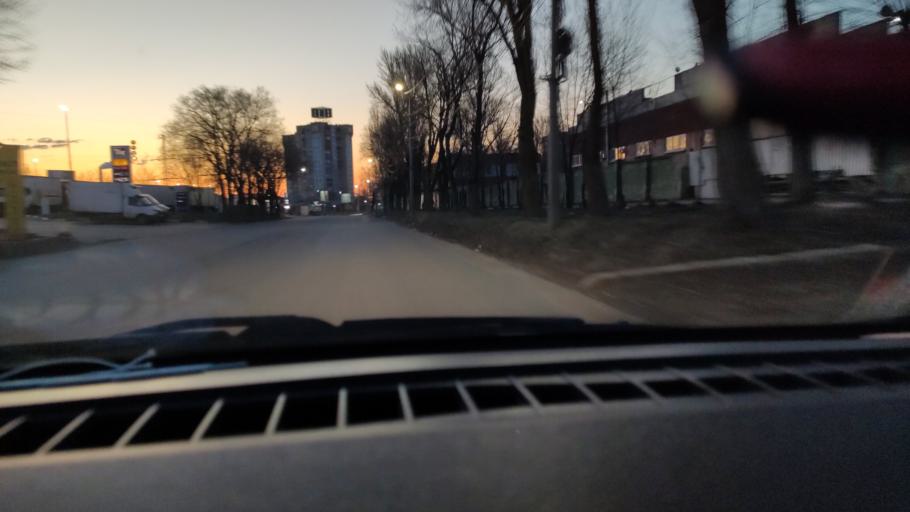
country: RU
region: Saratov
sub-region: Saratovskiy Rayon
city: Saratov
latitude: 51.6152
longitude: 45.9683
